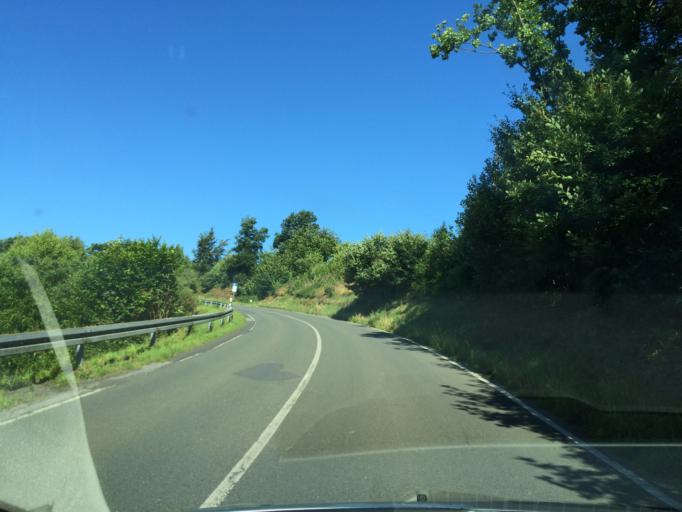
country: DE
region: North Rhine-Westphalia
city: Iserlohn
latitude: 51.3312
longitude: 7.7180
